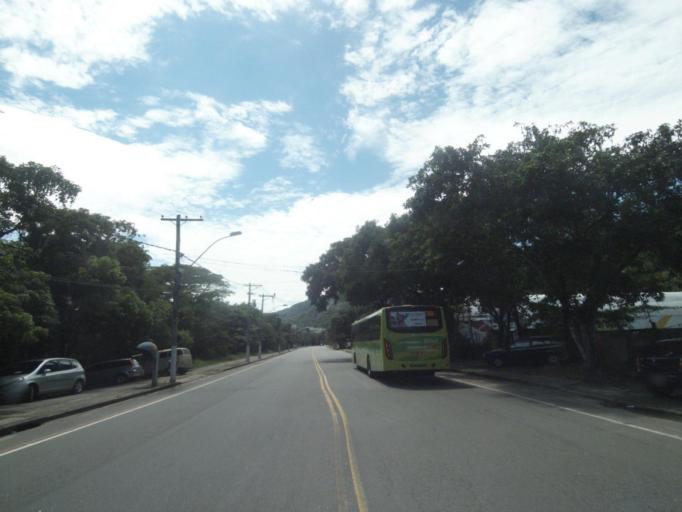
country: BR
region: Rio de Janeiro
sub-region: Niteroi
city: Niteroi
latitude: -22.9661
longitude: -43.0367
